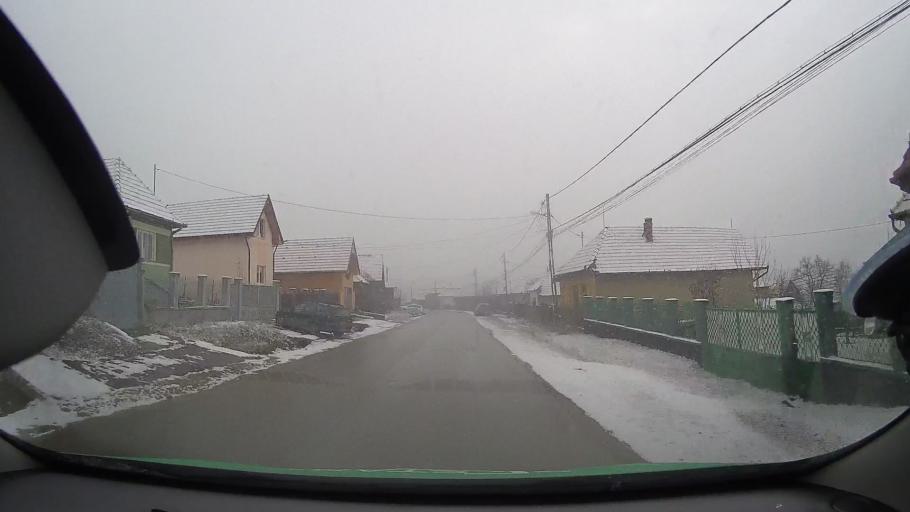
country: RO
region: Alba
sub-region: Comuna Lopadea Noua
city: Lopadea Noua
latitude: 46.2915
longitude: 23.8203
